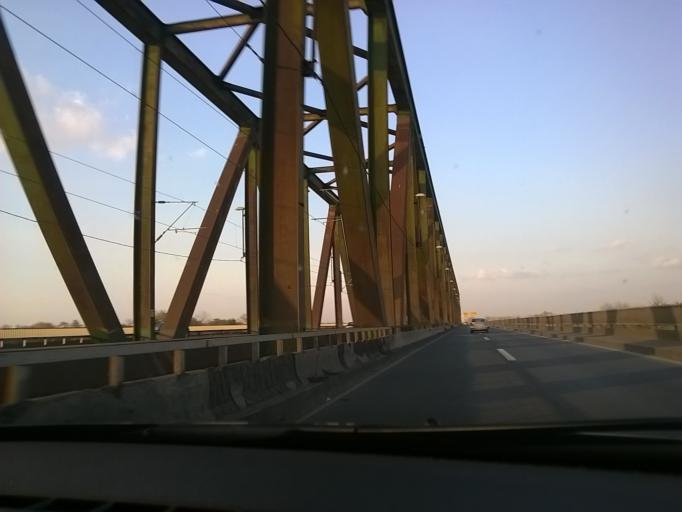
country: RS
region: Central Serbia
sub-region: Belgrade
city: Palilula
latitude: 44.8292
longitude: 20.4922
